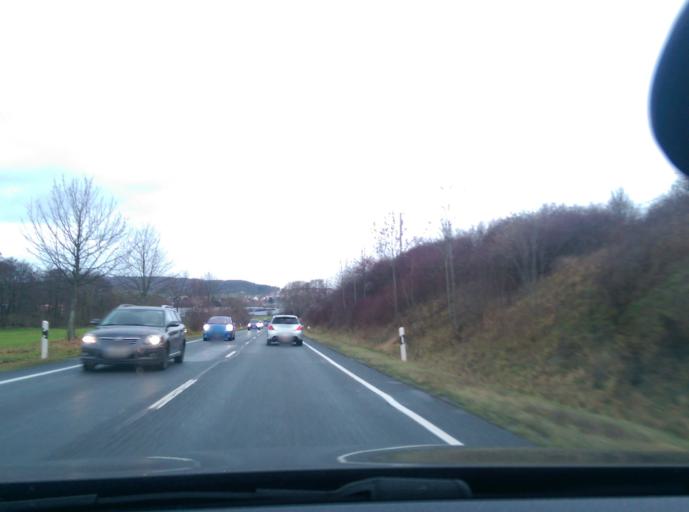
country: DE
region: Thuringia
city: Eisenach
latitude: 50.9984
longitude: 10.3342
